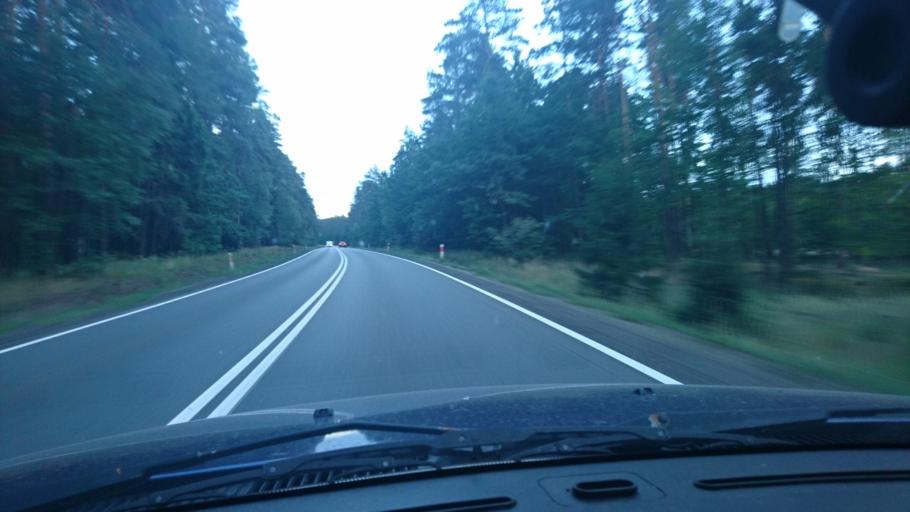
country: PL
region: Silesian Voivodeship
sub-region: Powiat tarnogorski
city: Tworog
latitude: 50.4968
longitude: 18.7717
